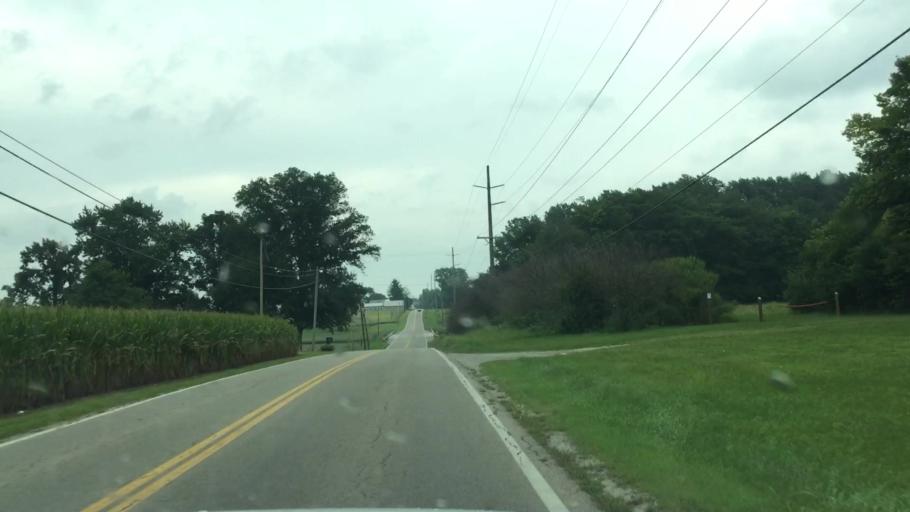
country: US
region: Ohio
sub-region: Clark County
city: Northridge
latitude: 39.9388
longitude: -83.7169
